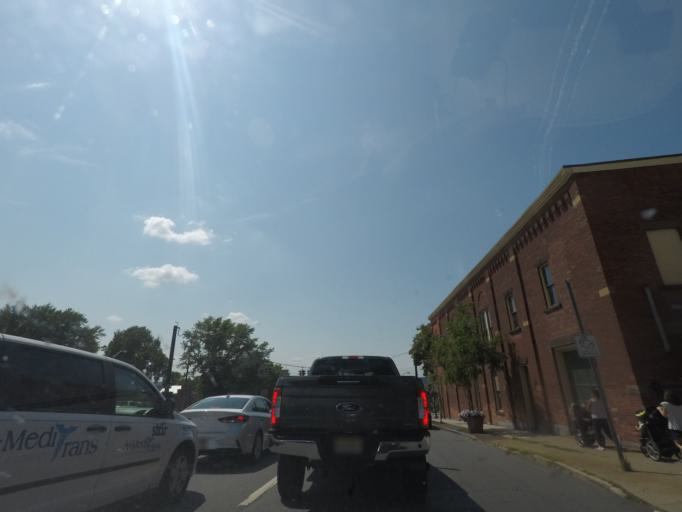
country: US
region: New York
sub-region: Albany County
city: Green Island
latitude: 42.7395
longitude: -73.6791
